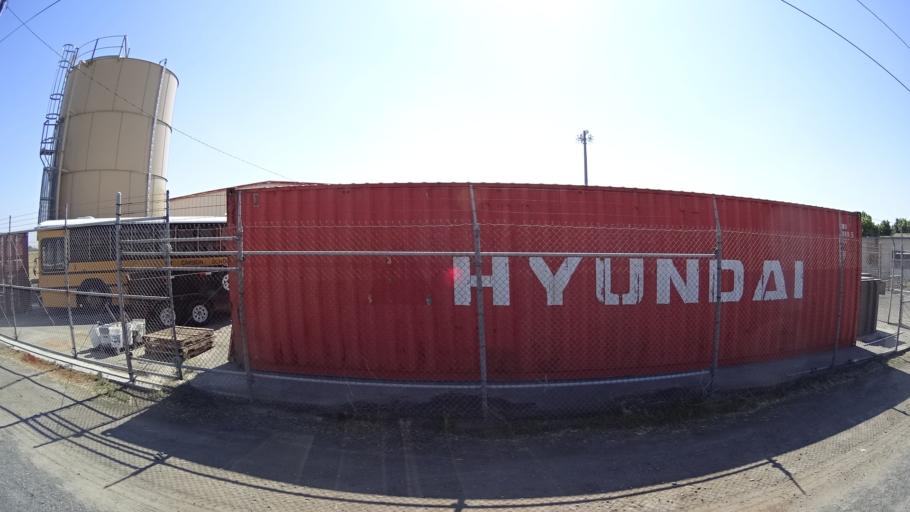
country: US
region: California
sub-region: Kings County
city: Home Garden
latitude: 36.3308
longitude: -119.5831
